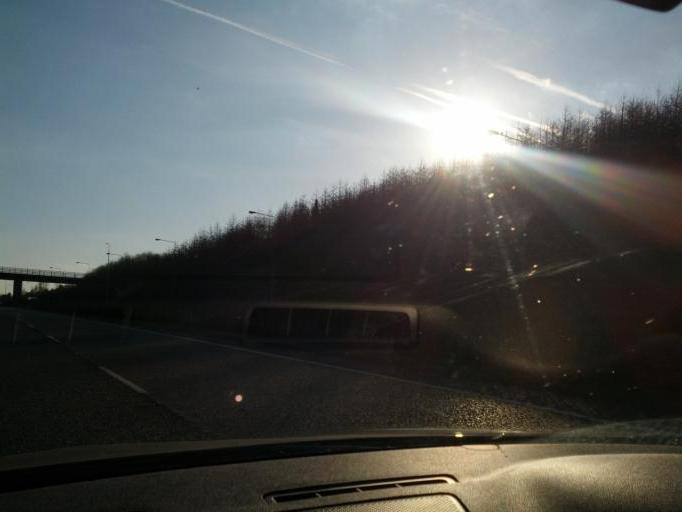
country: IE
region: Leinster
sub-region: Laois
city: Portlaoise
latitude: 53.0515
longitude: -7.2379
